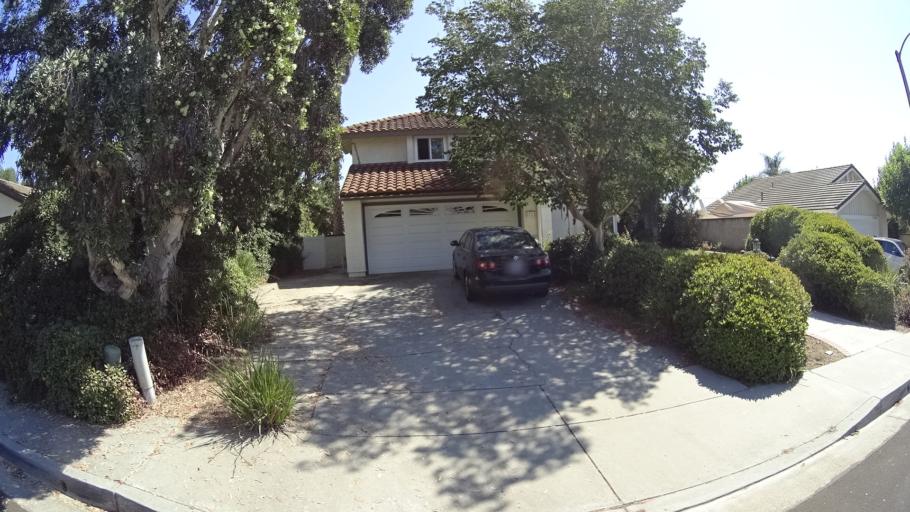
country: US
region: California
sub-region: Orange County
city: San Clemente
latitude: 33.4629
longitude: -117.6197
